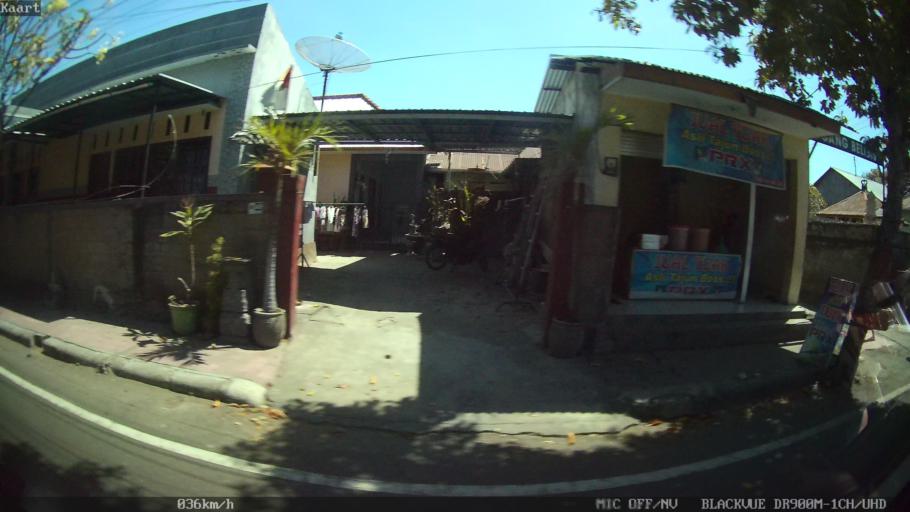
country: ID
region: Bali
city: Banjar Sidayu
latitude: -8.1009
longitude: 115.1194
